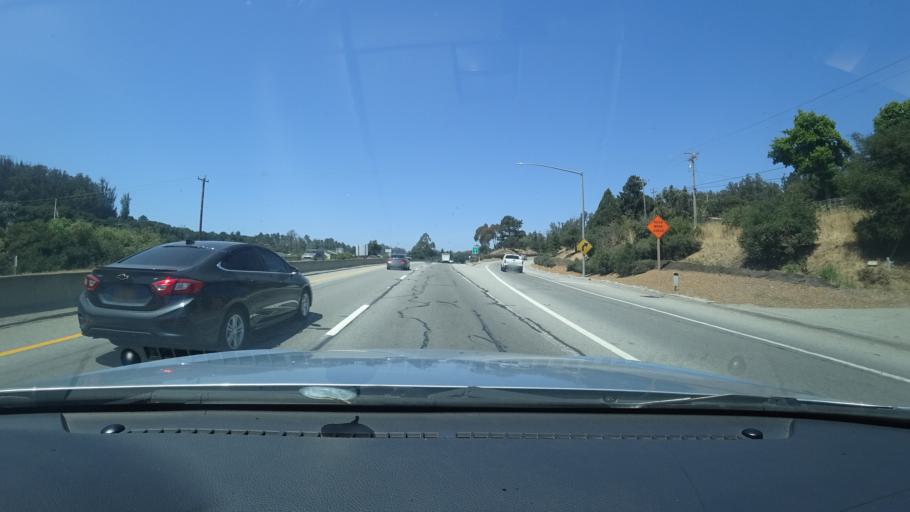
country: US
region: California
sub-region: Monterey County
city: Prunedale
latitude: 36.7948
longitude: -121.6664
